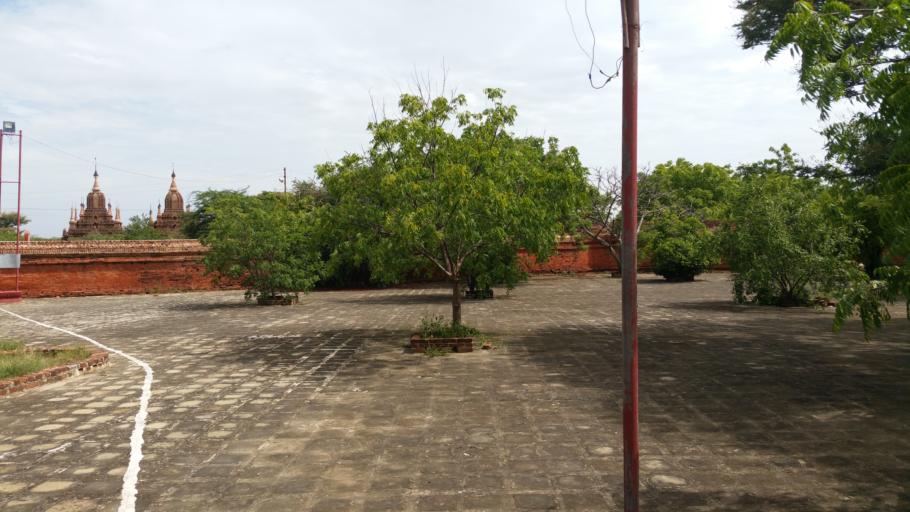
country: MM
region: Magway
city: Chauk
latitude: 21.1455
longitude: 94.8833
